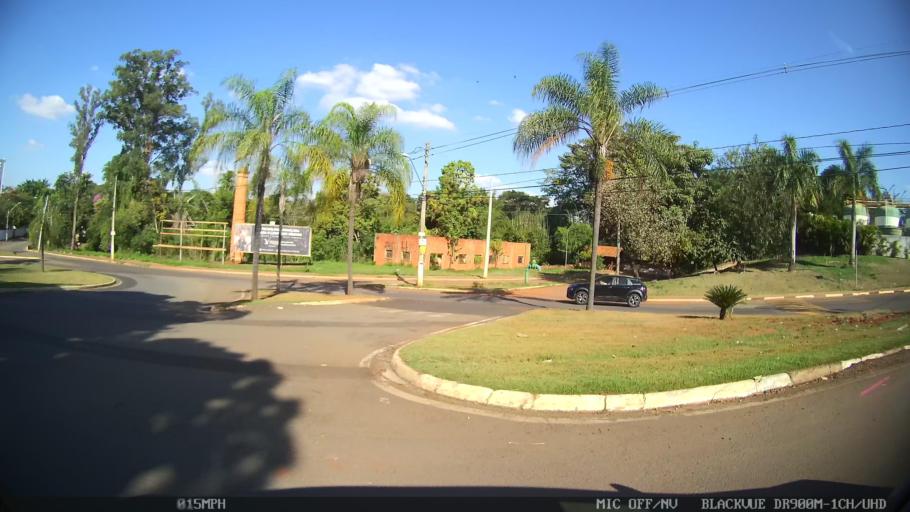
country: BR
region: Sao Paulo
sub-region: Sumare
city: Sumare
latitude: -22.8231
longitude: -47.2828
